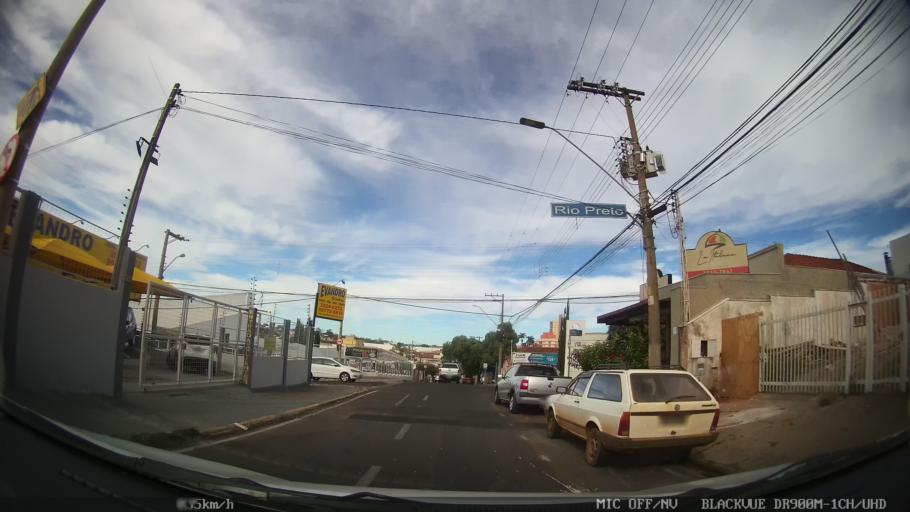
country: BR
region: Sao Paulo
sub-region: Catanduva
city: Catanduva
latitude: -21.1440
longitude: -48.9768
